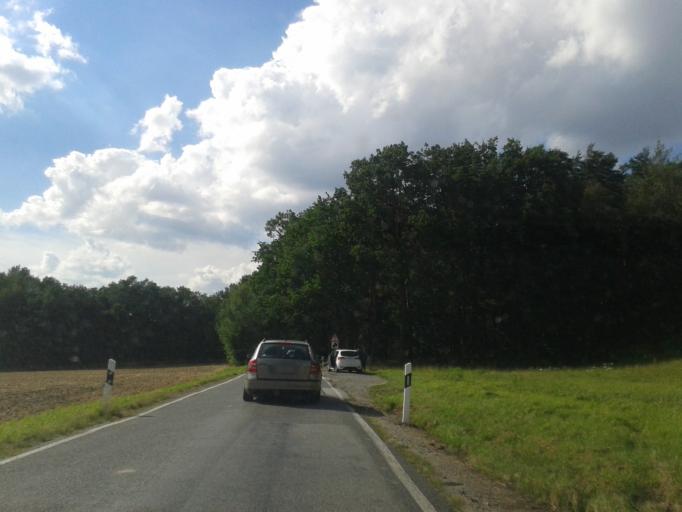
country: DE
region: Saxony
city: Radibor
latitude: 51.2026
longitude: 14.3802
